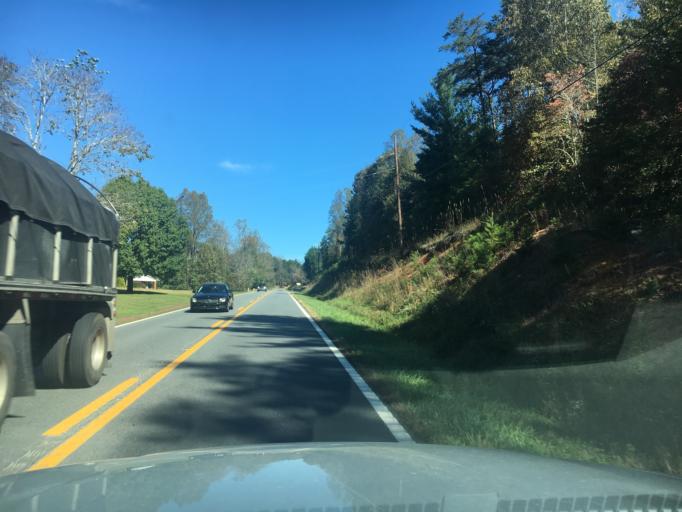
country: US
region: North Carolina
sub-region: Rutherford County
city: Spindale
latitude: 35.4948
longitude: -81.8659
